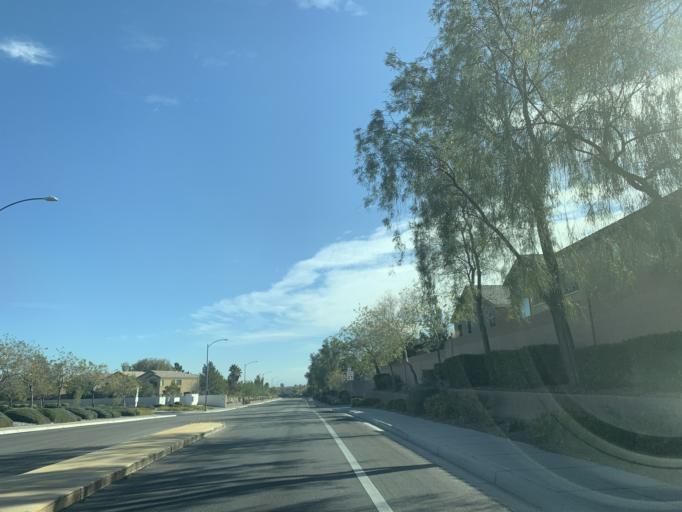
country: US
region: Nevada
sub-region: Clark County
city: Summerlin South
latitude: 36.3132
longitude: -115.2965
